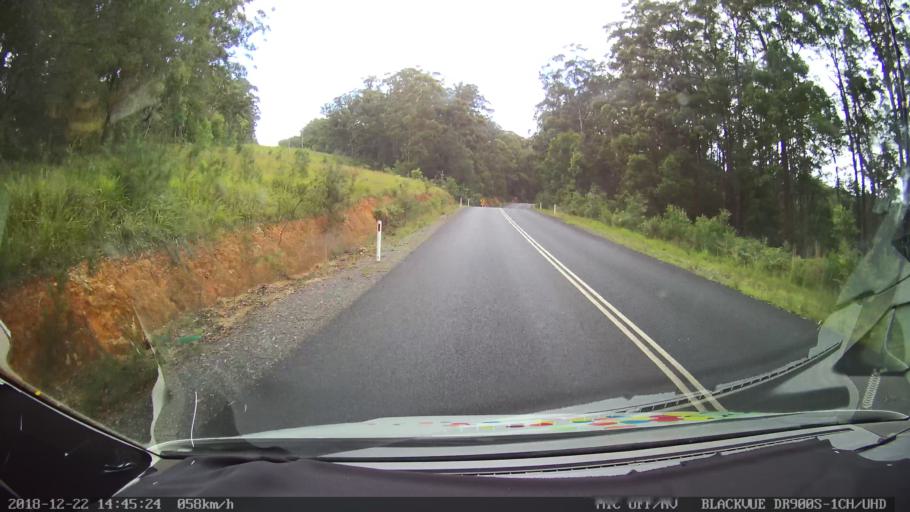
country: AU
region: New South Wales
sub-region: Bellingen
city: Dorrigo
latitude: -30.1700
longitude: 152.5695
